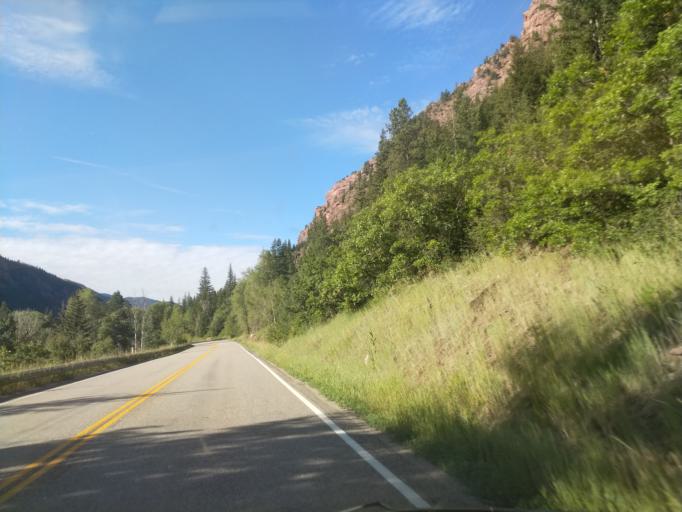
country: US
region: Colorado
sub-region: Garfield County
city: Carbondale
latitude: 39.2100
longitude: -107.2311
